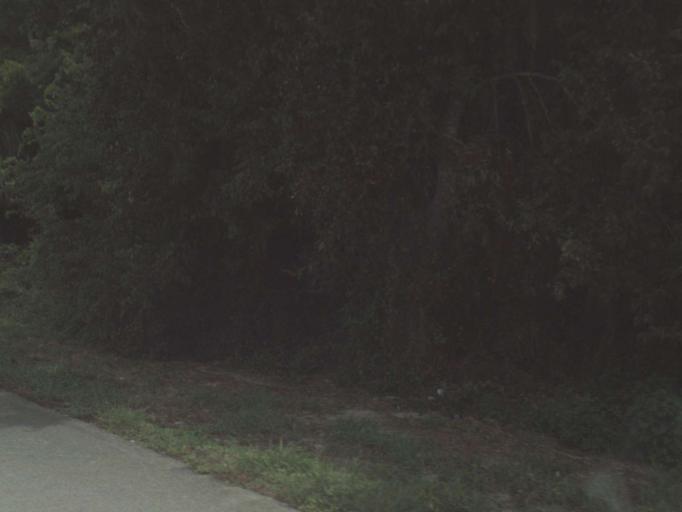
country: US
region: Florida
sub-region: Martin County
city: Indiantown
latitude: 27.0437
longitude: -80.6399
